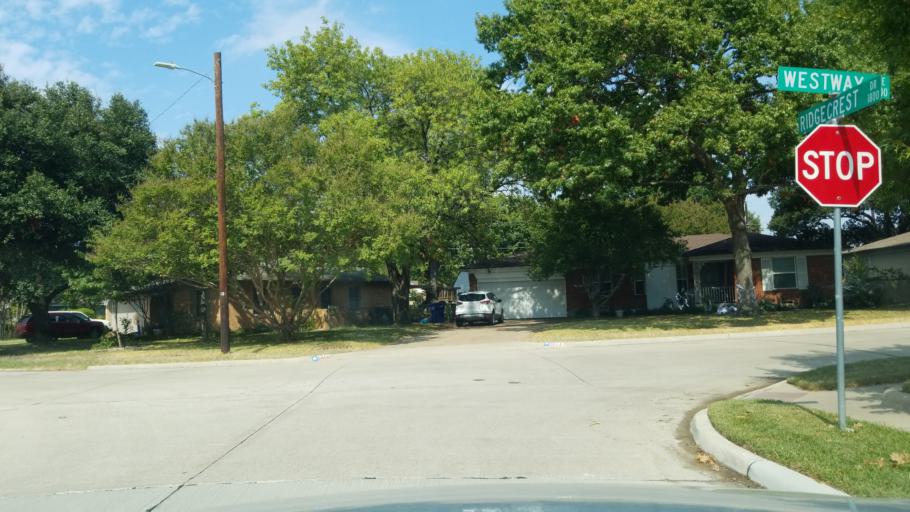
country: US
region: Texas
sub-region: Dallas County
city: Garland
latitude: 32.8973
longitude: -96.6578
